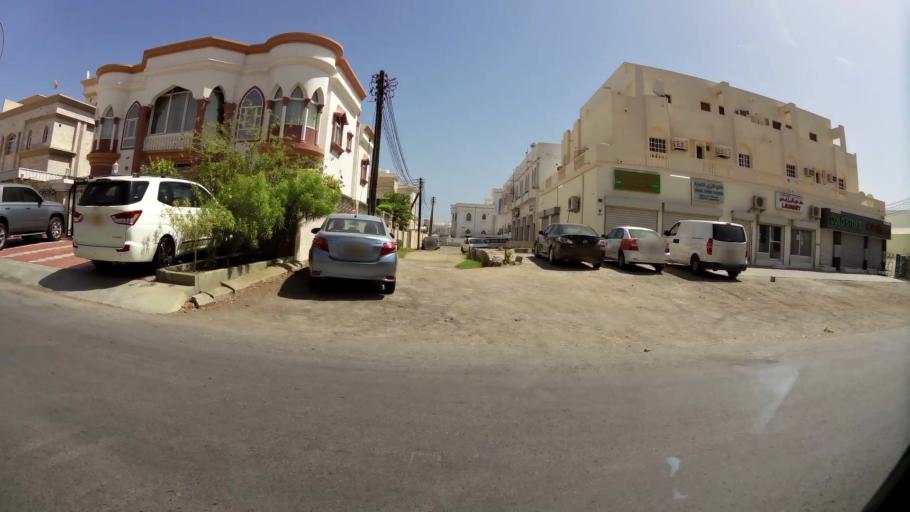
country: OM
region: Muhafazat Masqat
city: Bawshar
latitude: 23.5950
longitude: 58.4060
